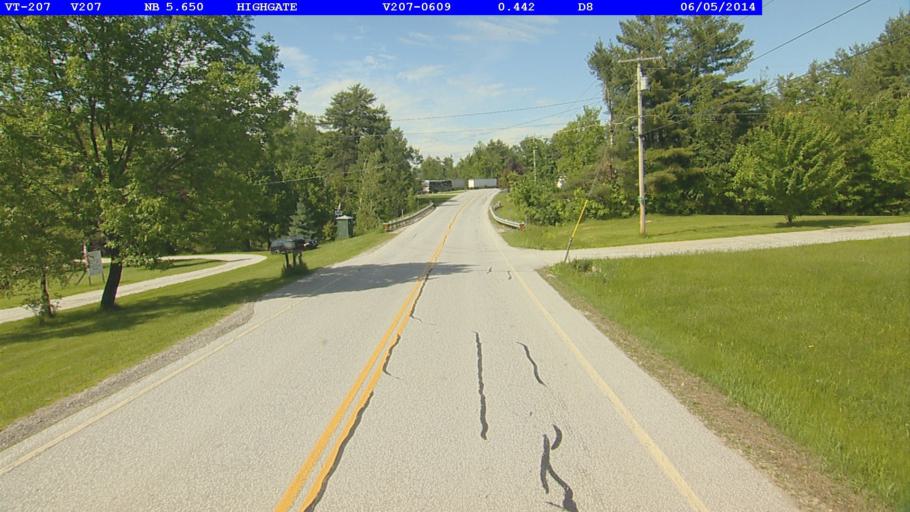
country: US
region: Vermont
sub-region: Franklin County
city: Swanton
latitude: 44.9178
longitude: -73.0557
